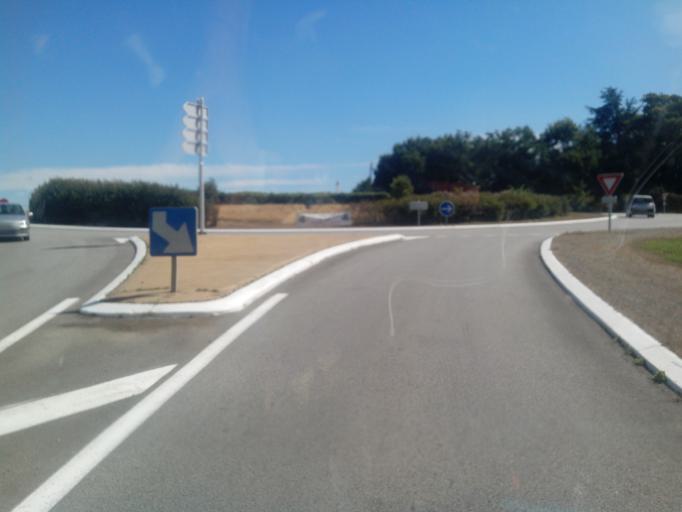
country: FR
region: Brittany
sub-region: Departement du Morbihan
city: Peaule
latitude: 47.5397
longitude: -2.3984
